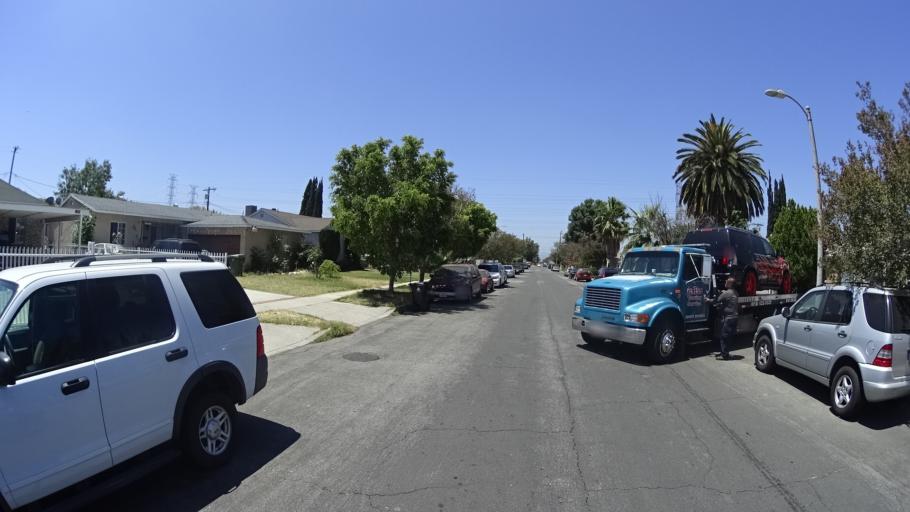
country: US
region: California
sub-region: Los Angeles County
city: San Fernando
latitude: 34.2378
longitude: -118.4303
